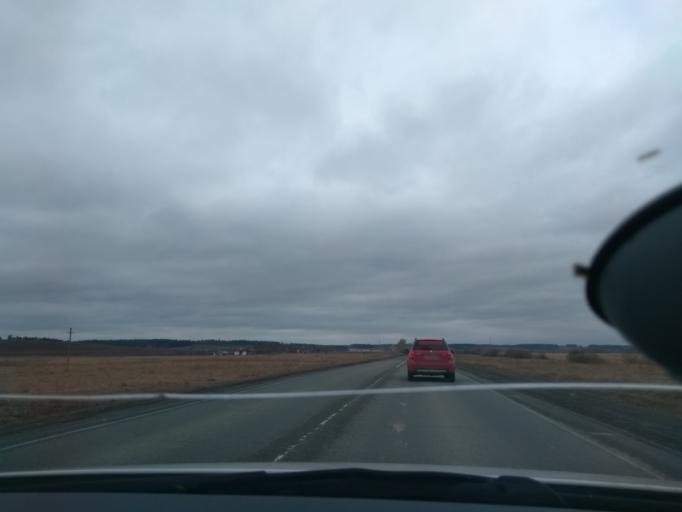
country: RU
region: Perm
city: Kukushtan
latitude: 57.4992
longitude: 56.6563
